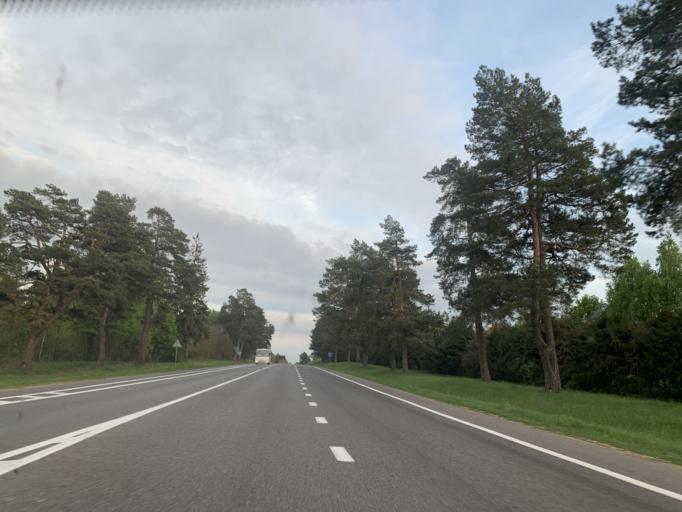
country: BY
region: Minsk
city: Haradzyeya
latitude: 53.2704
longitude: 26.6005
